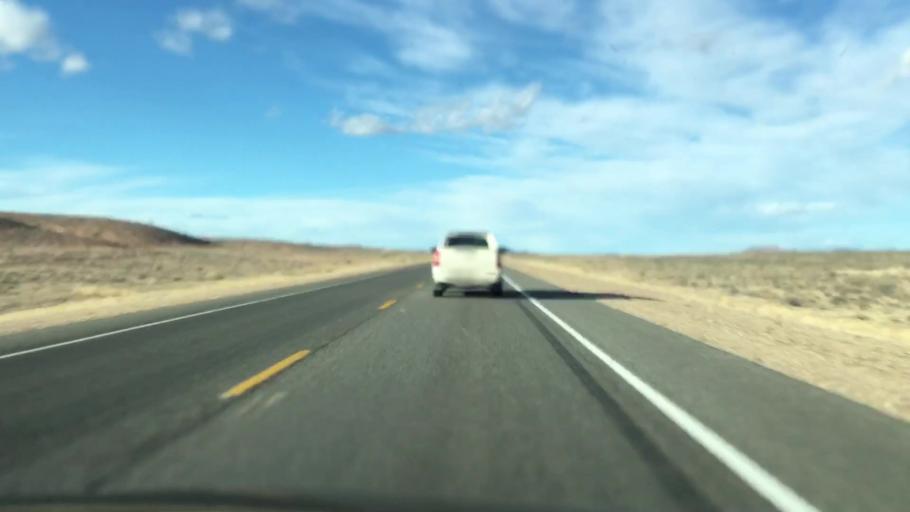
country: US
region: Nevada
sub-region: Esmeralda County
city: Goldfield
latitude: 37.5611
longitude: -117.1989
